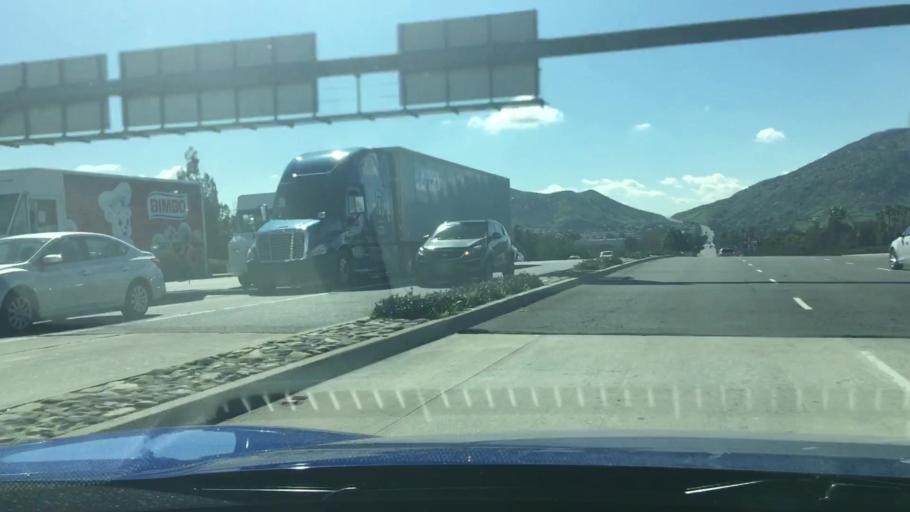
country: US
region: California
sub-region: San Bernardino County
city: Fontana
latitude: 34.0665
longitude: -117.4357
